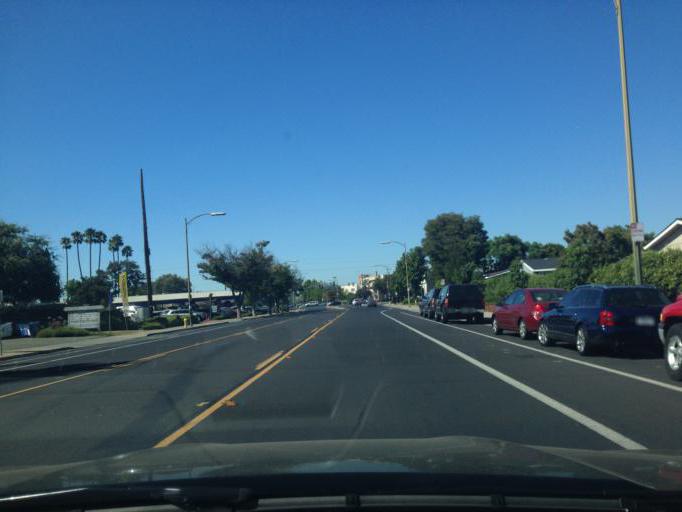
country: US
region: California
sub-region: Santa Clara County
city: Seven Trees
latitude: 37.2485
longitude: -121.8671
